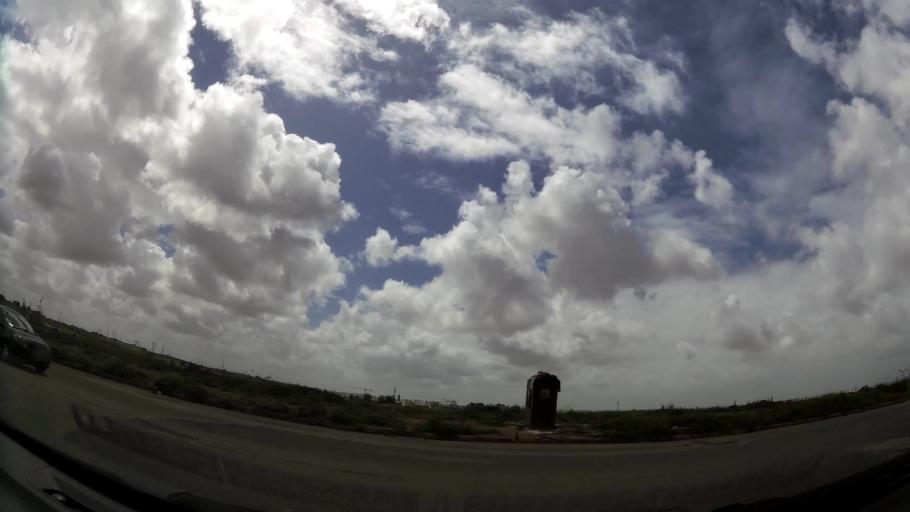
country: MA
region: Grand Casablanca
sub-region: Casablanca
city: Casablanca
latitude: 33.5236
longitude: -7.6005
